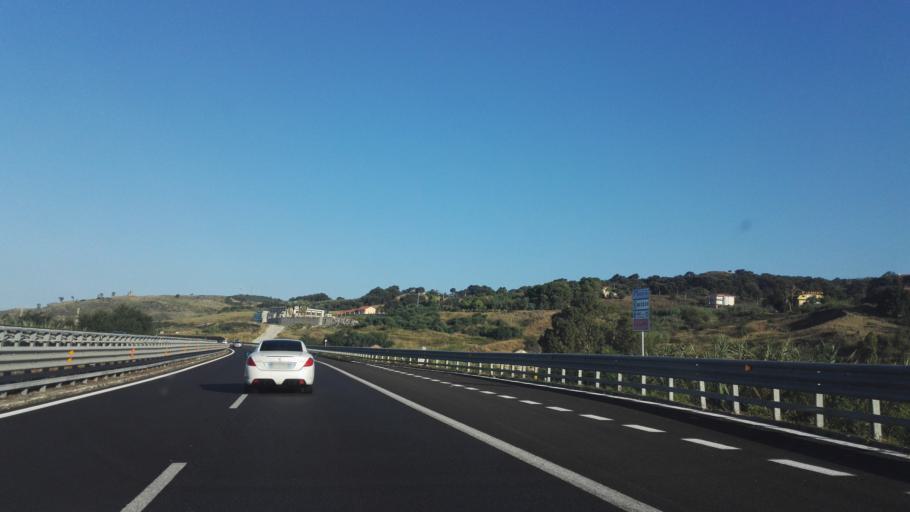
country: IT
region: Calabria
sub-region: Provincia di Catanzaro
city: Gizzeria
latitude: 38.9485
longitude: 16.1840
